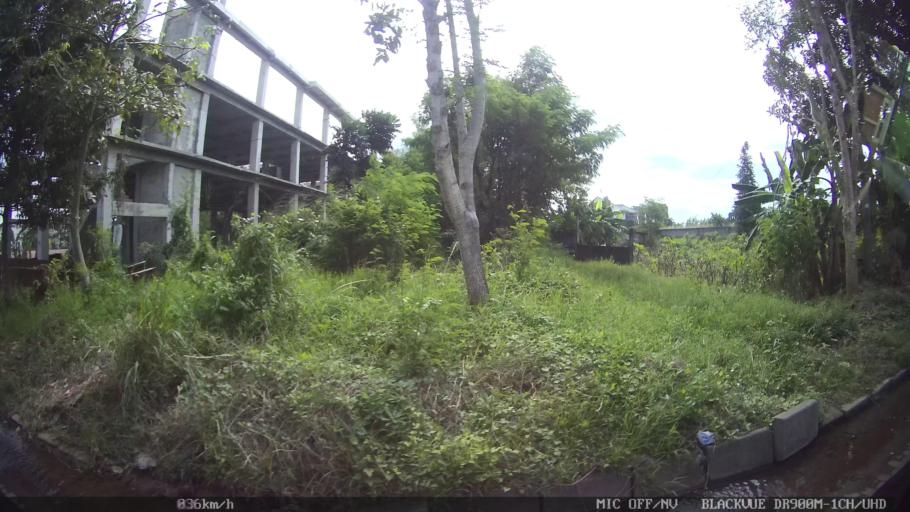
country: ID
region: Daerah Istimewa Yogyakarta
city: Depok
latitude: -7.7589
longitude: 110.4191
